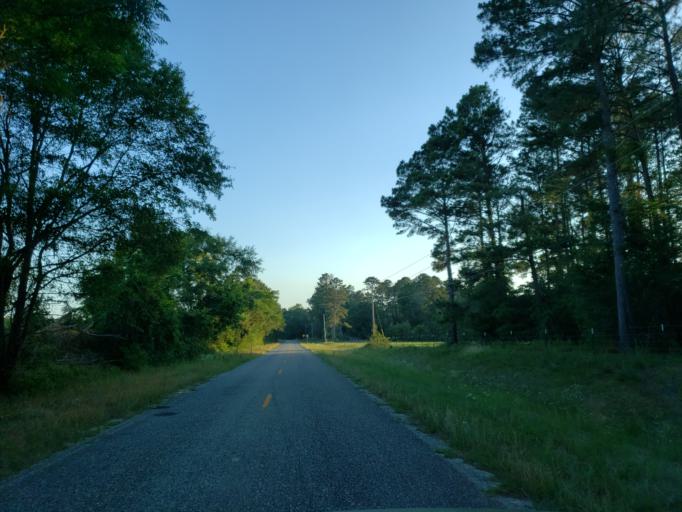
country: US
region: Georgia
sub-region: Crisp County
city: Cordele
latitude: 32.0226
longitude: -83.7513
